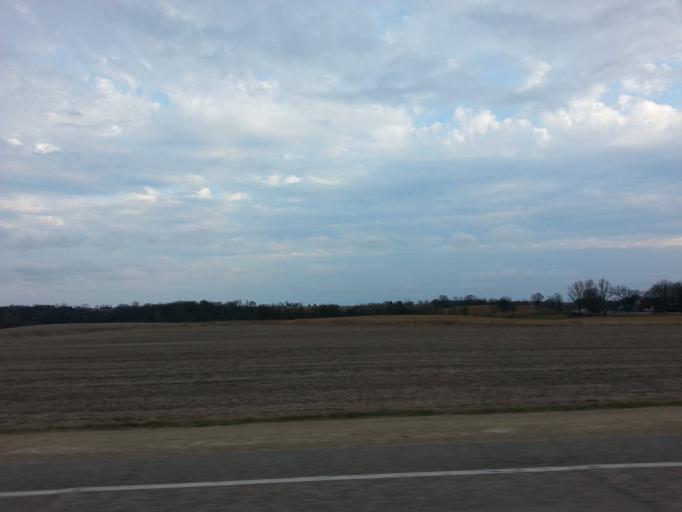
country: US
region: Wisconsin
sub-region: Pierce County
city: Ellsworth
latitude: 44.7302
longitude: -92.5603
